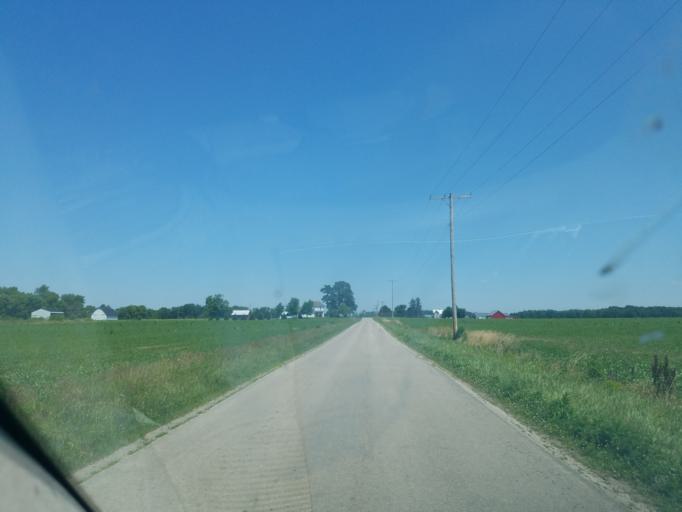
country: US
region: Ohio
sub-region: Mercer County
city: Rockford
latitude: 40.7383
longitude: -84.7370
